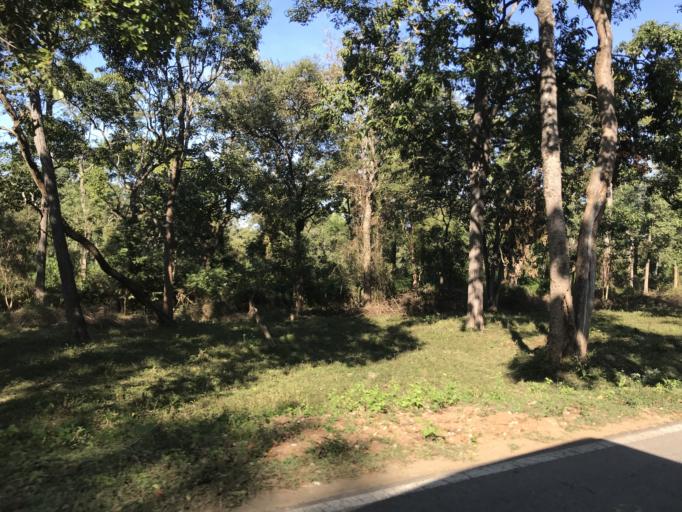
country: IN
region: Karnataka
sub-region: Mysore
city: Heggadadevankote
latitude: 11.9449
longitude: 76.2334
